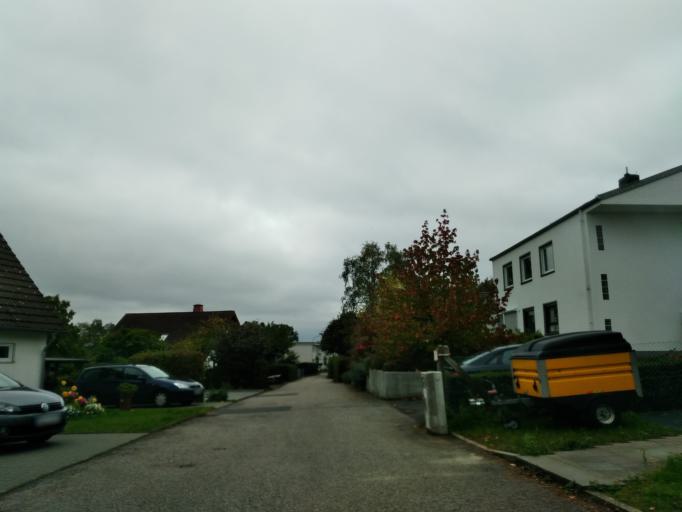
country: DE
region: Rheinland-Pfalz
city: Windhagen
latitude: 50.6601
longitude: 7.2999
